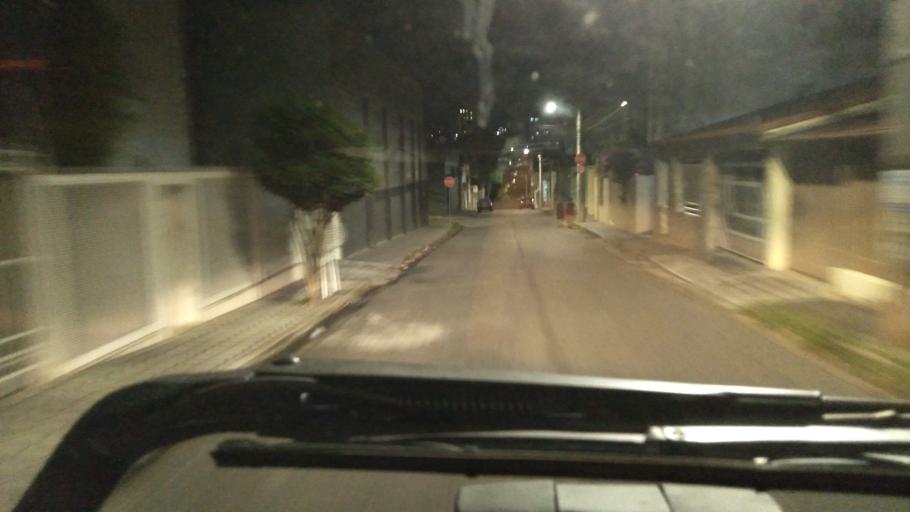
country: BR
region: Minas Gerais
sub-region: Belo Horizonte
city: Belo Horizonte
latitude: -19.9215
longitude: -43.9778
